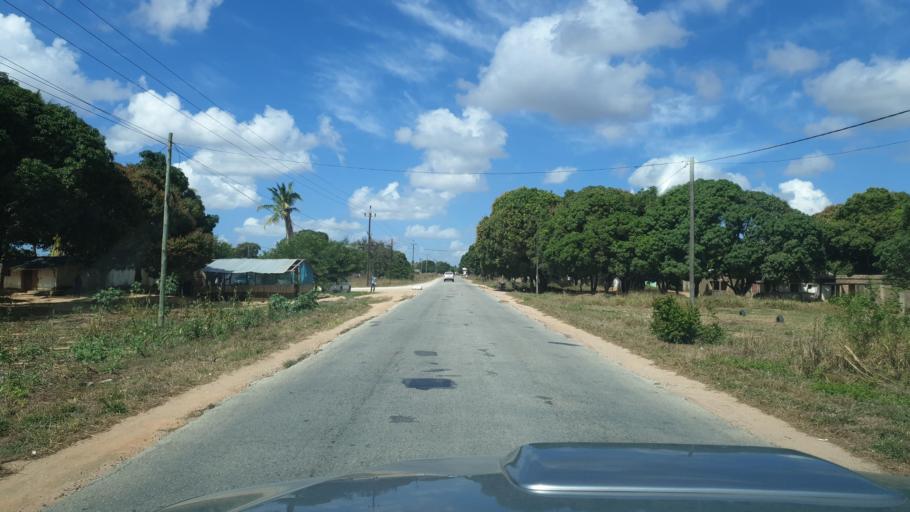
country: MZ
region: Nampula
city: Nacala
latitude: -14.5022
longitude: 40.6970
